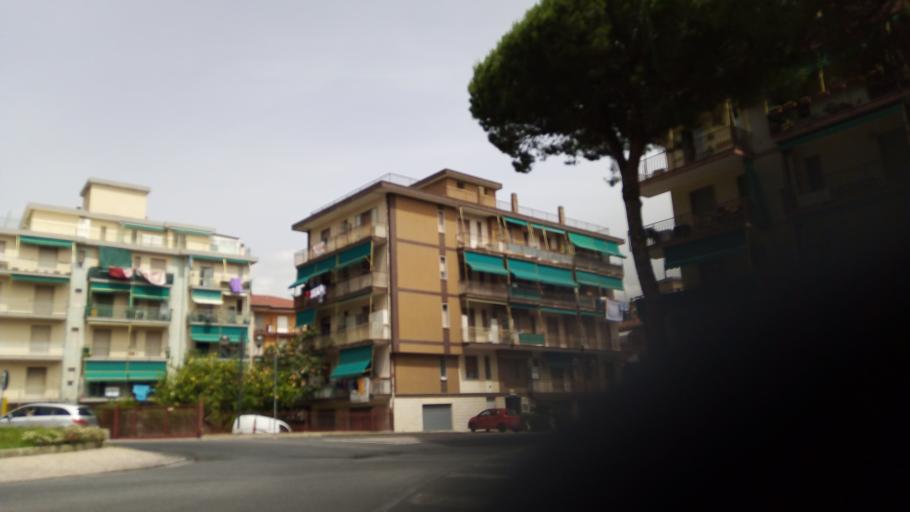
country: IT
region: Liguria
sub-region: Provincia di Savona
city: Borghetto Santo Spirito
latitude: 44.1114
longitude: 8.2382
